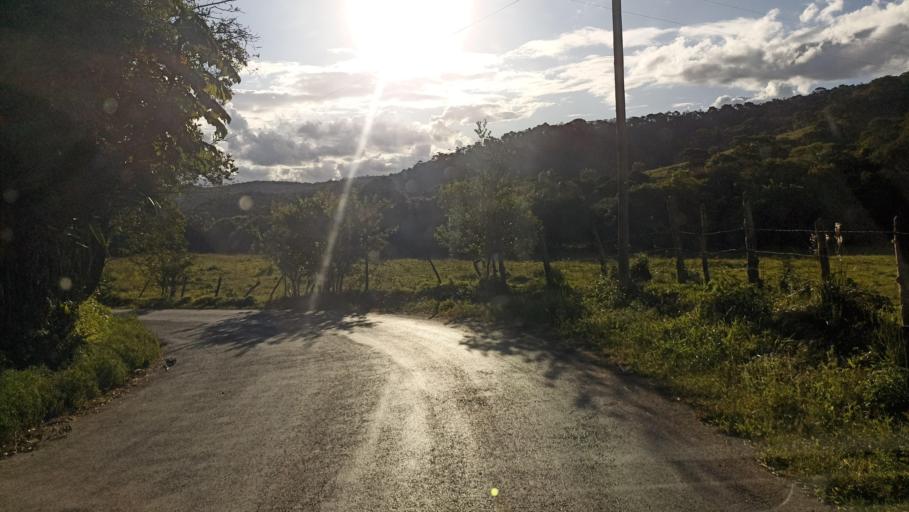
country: BR
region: Minas Gerais
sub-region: Ouro Preto
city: Ouro Preto
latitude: -20.3094
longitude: -43.6036
